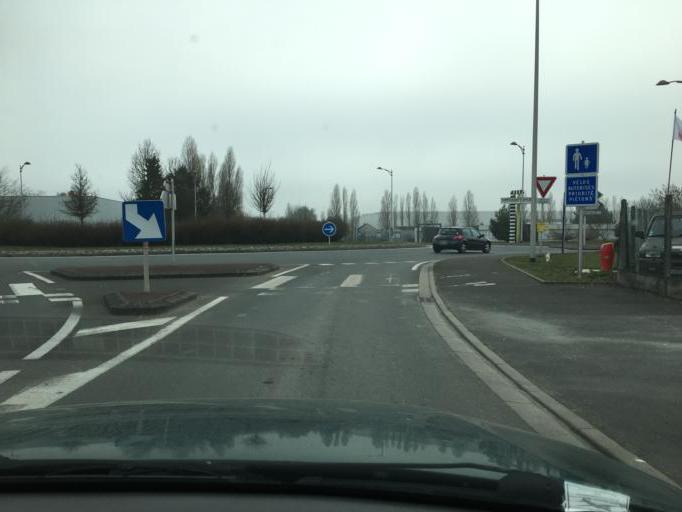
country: FR
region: Centre
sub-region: Departement du Loiret
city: Ormes
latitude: 47.9486
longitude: 1.8308
